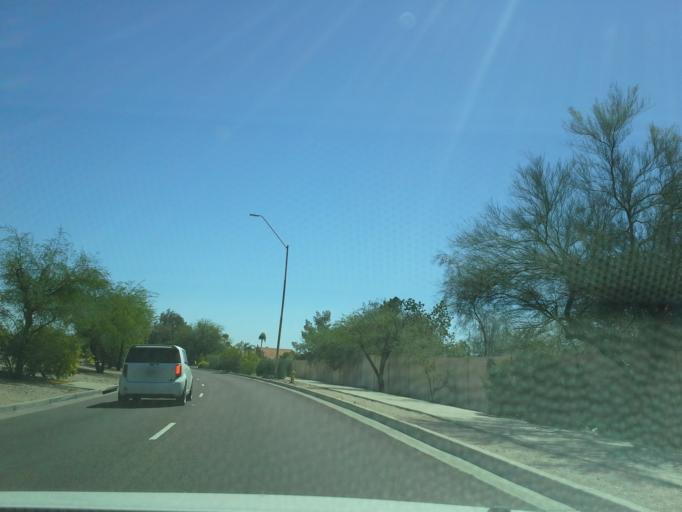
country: US
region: Arizona
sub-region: Maricopa County
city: Scottsdale
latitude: 33.6037
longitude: -111.8544
